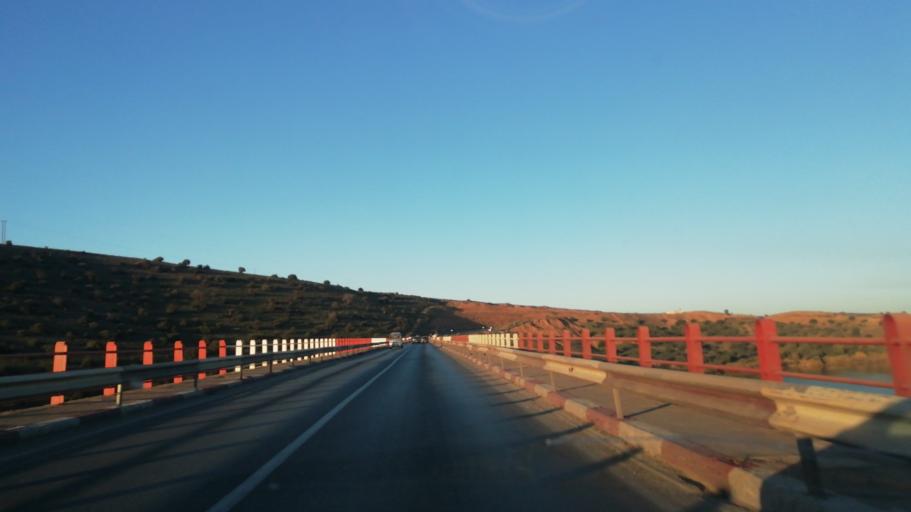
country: DZ
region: Tlemcen
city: Nedroma
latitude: 34.8865
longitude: -1.6697
